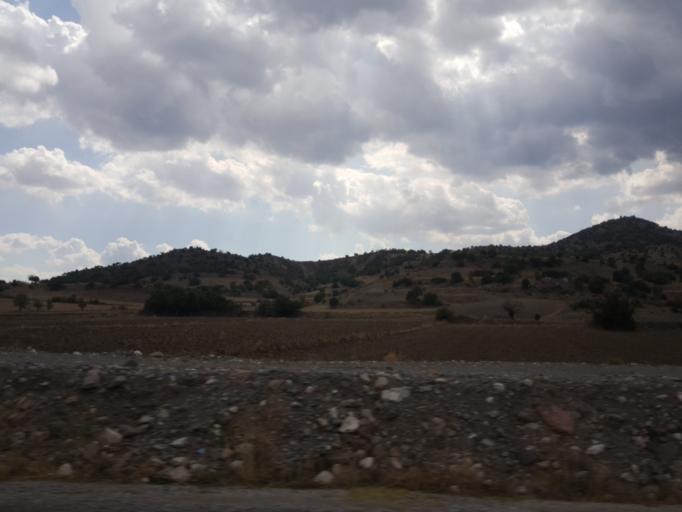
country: TR
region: Yozgat
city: Cekerek
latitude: 40.1921
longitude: 35.4226
